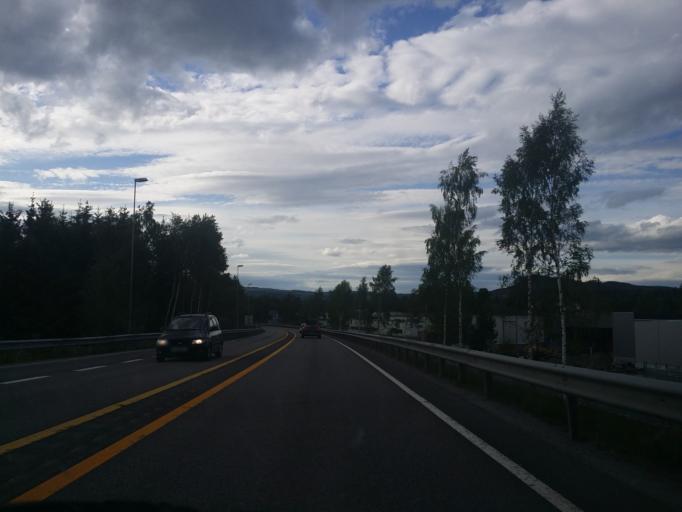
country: NO
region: Hedmark
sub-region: Ringsaker
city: Brumunddal
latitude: 60.8703
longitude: 10.9476
